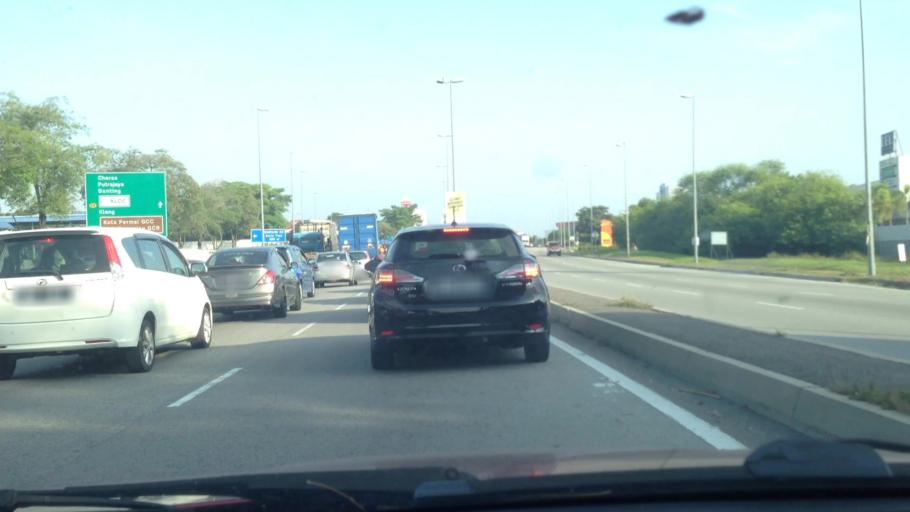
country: MY
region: Selangor
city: Subang Jaya
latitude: 3.0440
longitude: 101.5461
